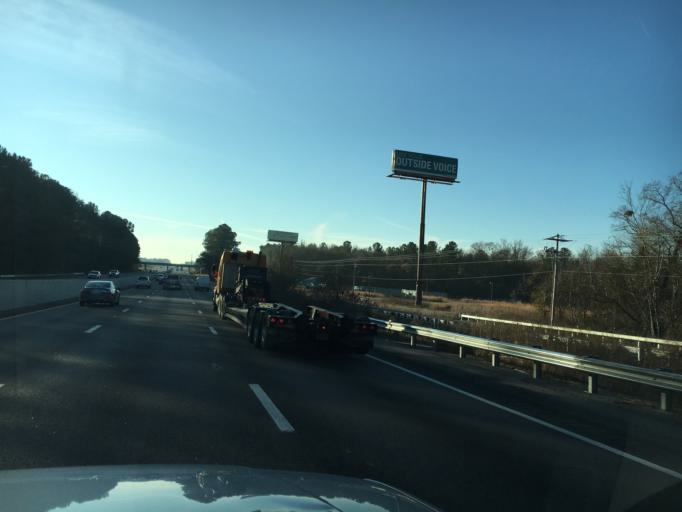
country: US
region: South Carolina
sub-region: Lexington County
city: Gaston
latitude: 33.8538
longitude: -81.0282
